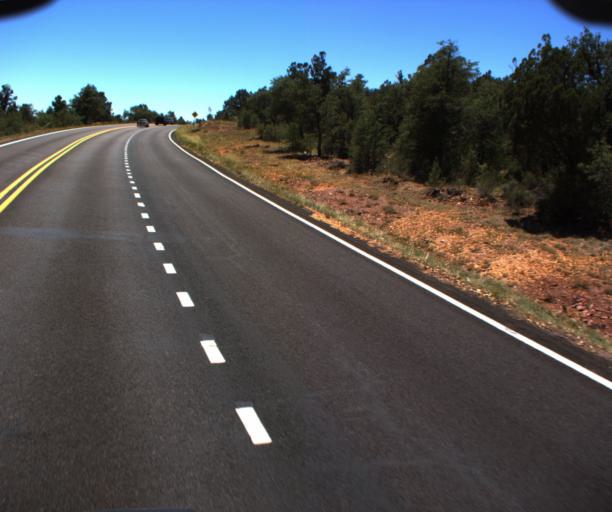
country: US
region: Arizona
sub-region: Gila County
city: Pine
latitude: 34.3587
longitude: -111.4245
